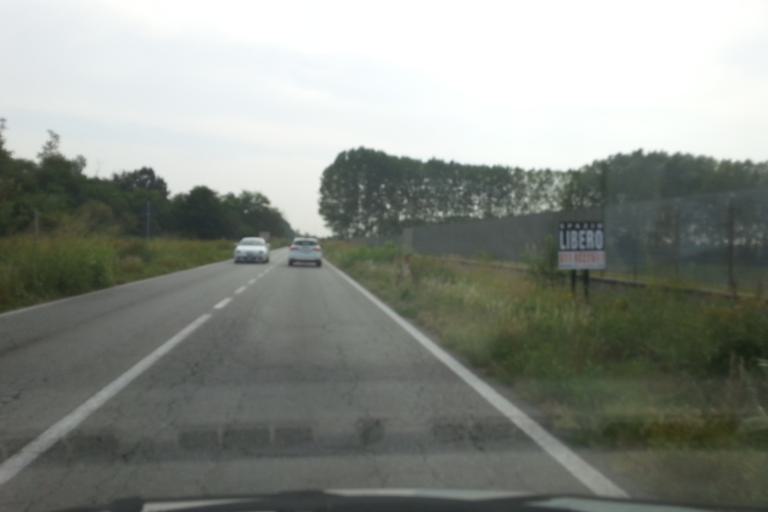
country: IT
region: Piedmont
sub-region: Provincia di Torino
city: Pasta
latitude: 45.0274
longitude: 7.5452
